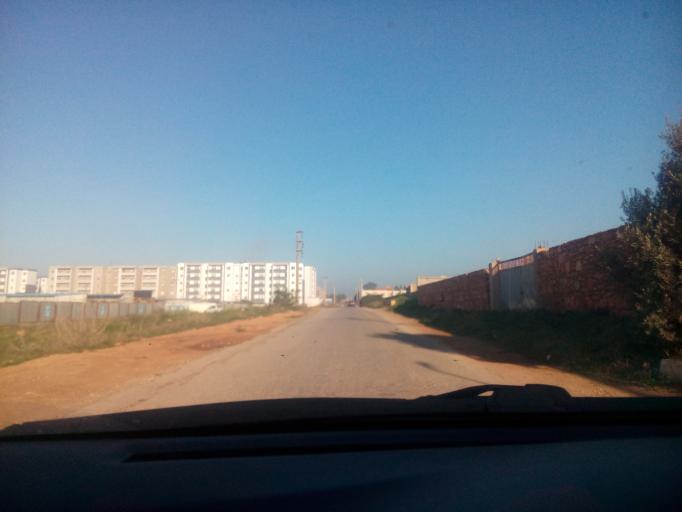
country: DZ
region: Oran
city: Bir el Djir
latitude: 35.7523
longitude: -0.5290
